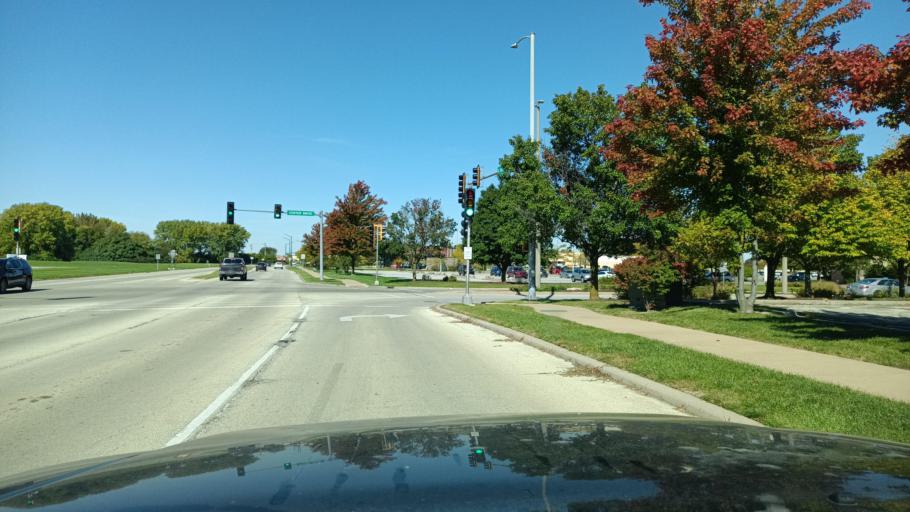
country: US
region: Illinois
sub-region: Champaign County
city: Champaign
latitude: 40.1398
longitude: -88.2444
